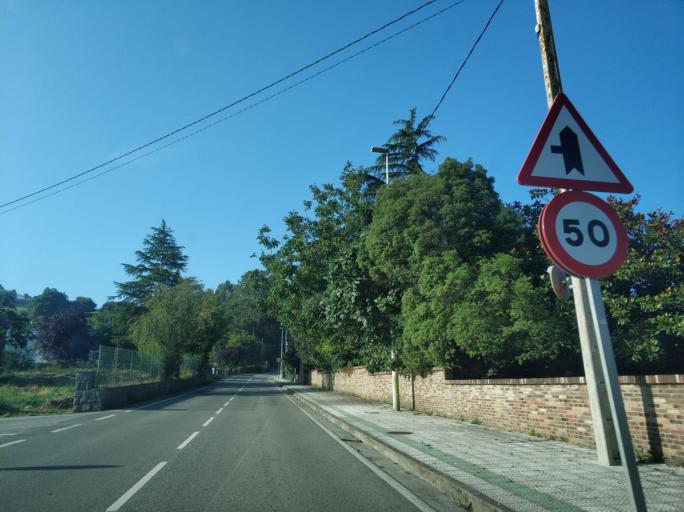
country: ES
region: Cantabria
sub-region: Provincia de Cantabria
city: Camargo
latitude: 43.4007
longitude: -3.9418
